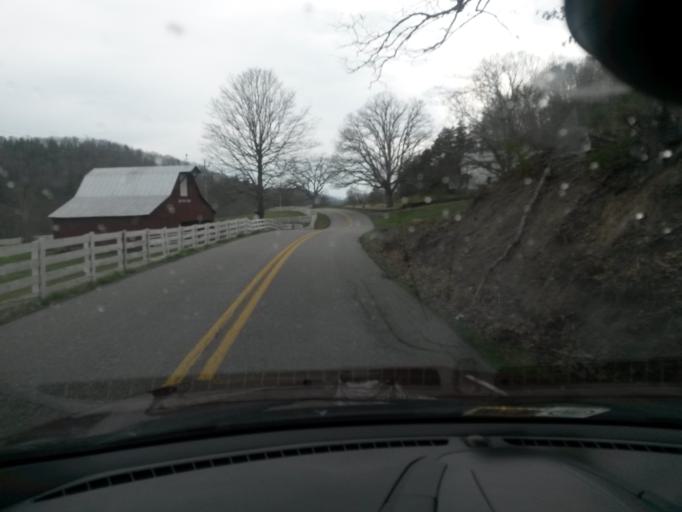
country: US
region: Virginia
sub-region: Bath County
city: Warm Springs
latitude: 37.9858
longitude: -79.9018
